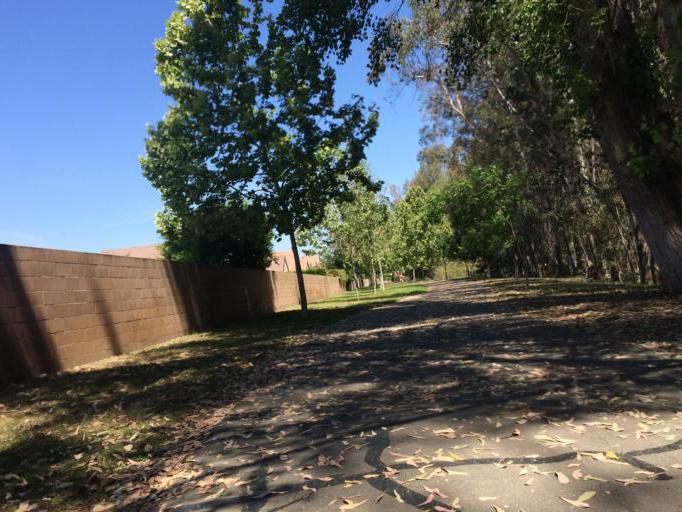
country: US
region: California
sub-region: Fresno County
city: Clovis
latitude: 36.8610
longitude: -119.7001
